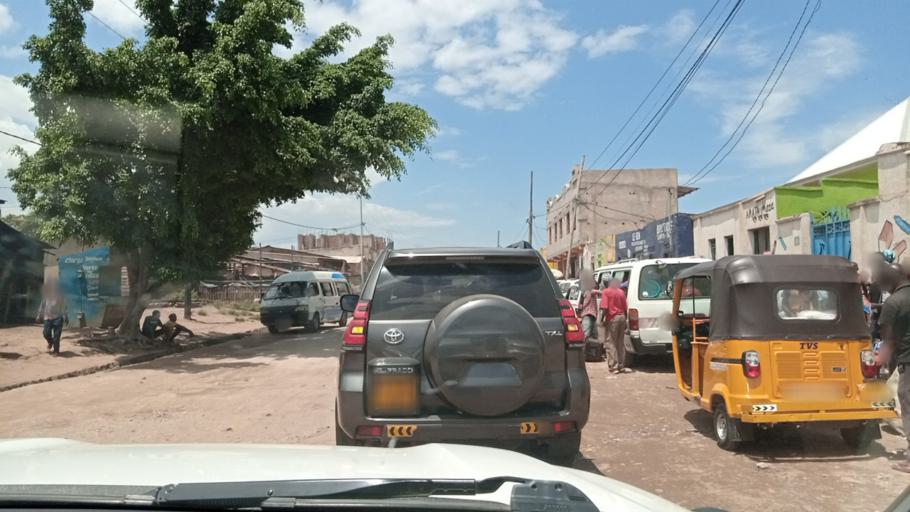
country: BI
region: Bujumbura Mairie
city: Bujumbura
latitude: -3.4264
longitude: 29.3553
